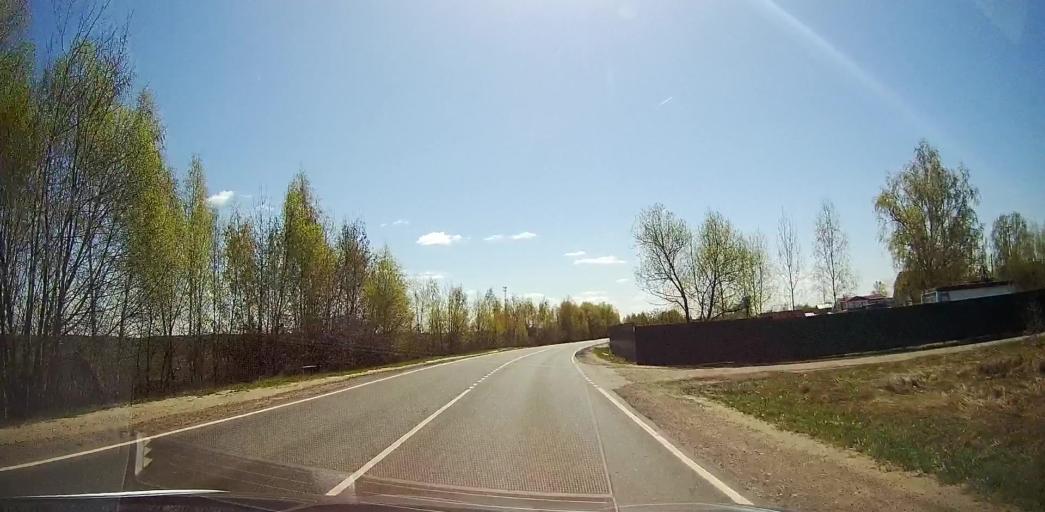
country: RU
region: Moskovskaya
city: Beloozerskiy
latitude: 55.5213
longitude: 38.4351
